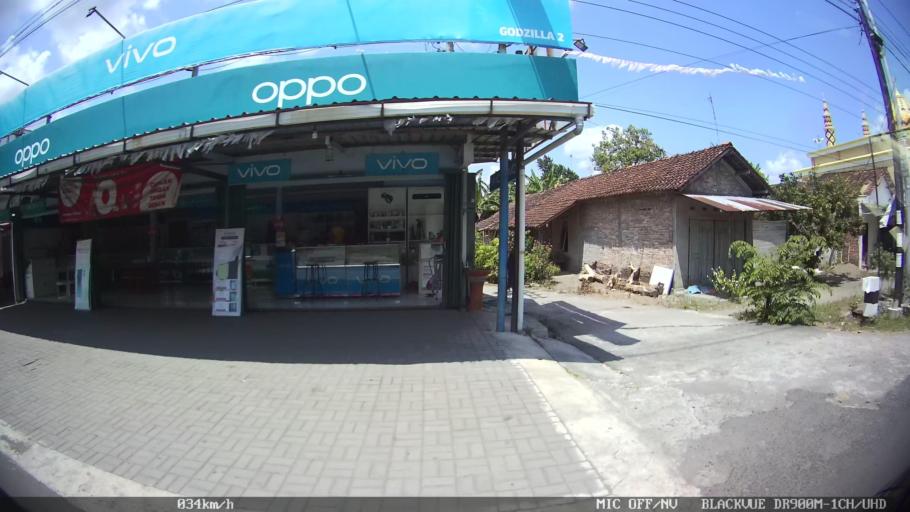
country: ID
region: Daerah Istimewa Yogyakarta
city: Sewon
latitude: -7.9010
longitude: 110.3840
